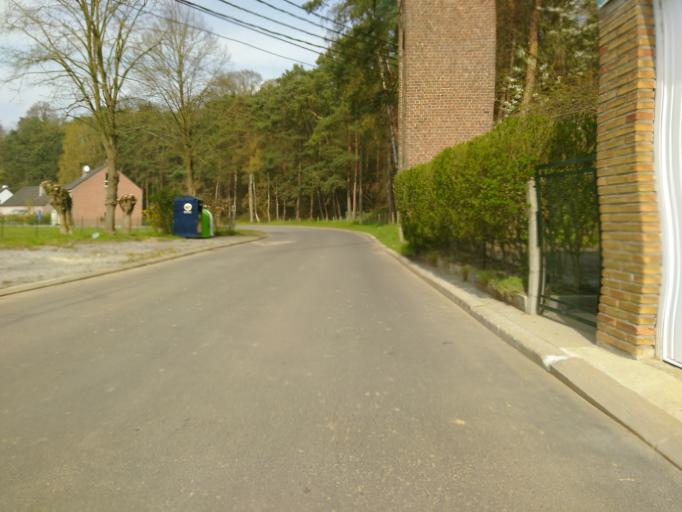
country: BE
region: Wallonia
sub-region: Province du Brabant Wallon
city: Chaumont-Gistoux
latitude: 50.6808
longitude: 4.7229
